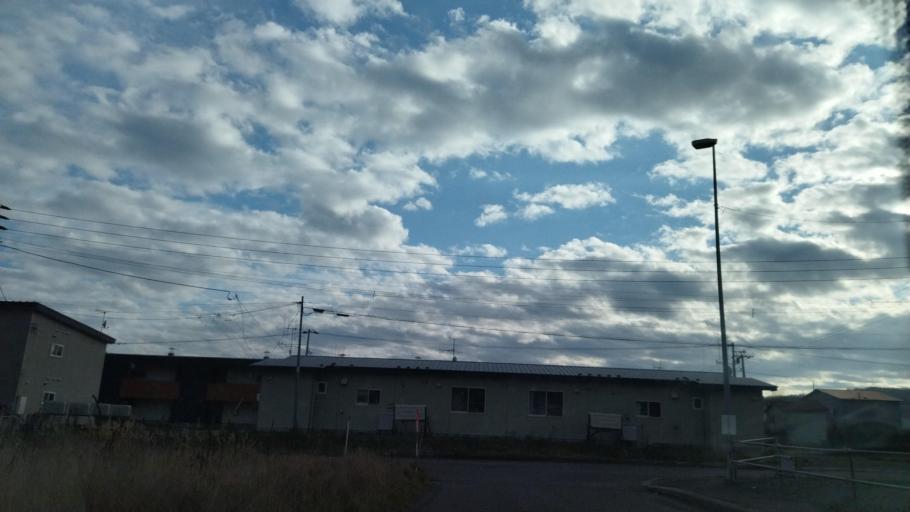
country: JP
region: Hokkaido
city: Otofuke
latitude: 43.2470
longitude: 143.5505
